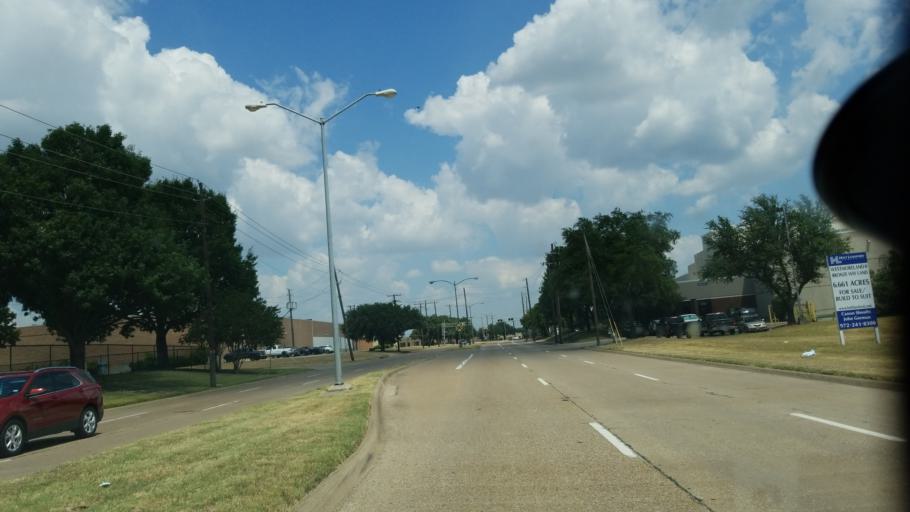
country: US
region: Texas
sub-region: Dallas County
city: Duncanville
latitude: 32.6845
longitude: -96.8828
